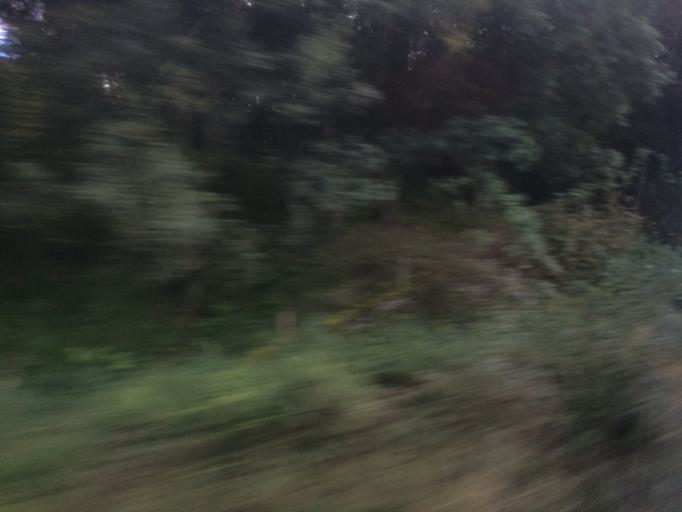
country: GB
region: Scotland
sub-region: North Lanarkshire
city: Cumbernauld
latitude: 55.9715
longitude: -4.0049
